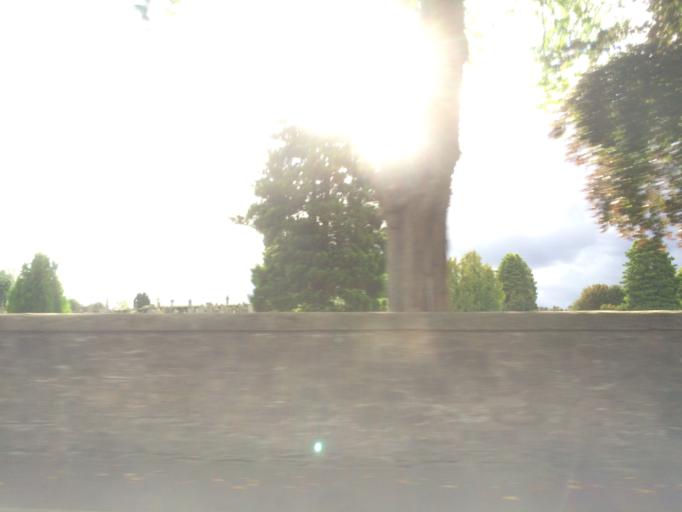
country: GB
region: Scotland
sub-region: Perth and Kinross
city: Perth
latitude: 56.4005
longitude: -3.4464
